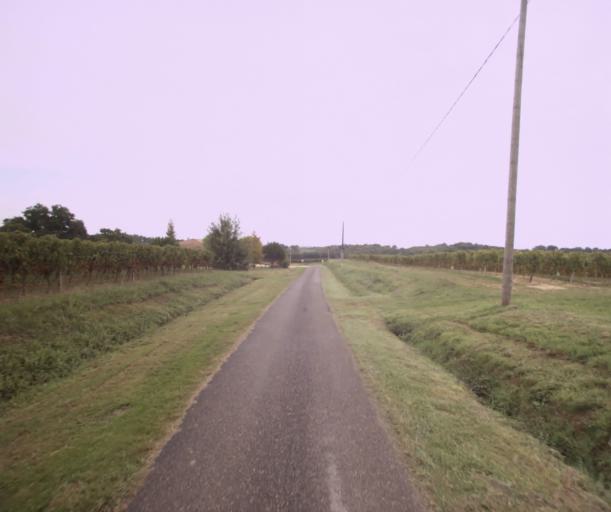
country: FR
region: Midi-Pyrenees
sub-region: Departement du Gers
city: Cazaubon
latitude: 43.8709
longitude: -0.0577
